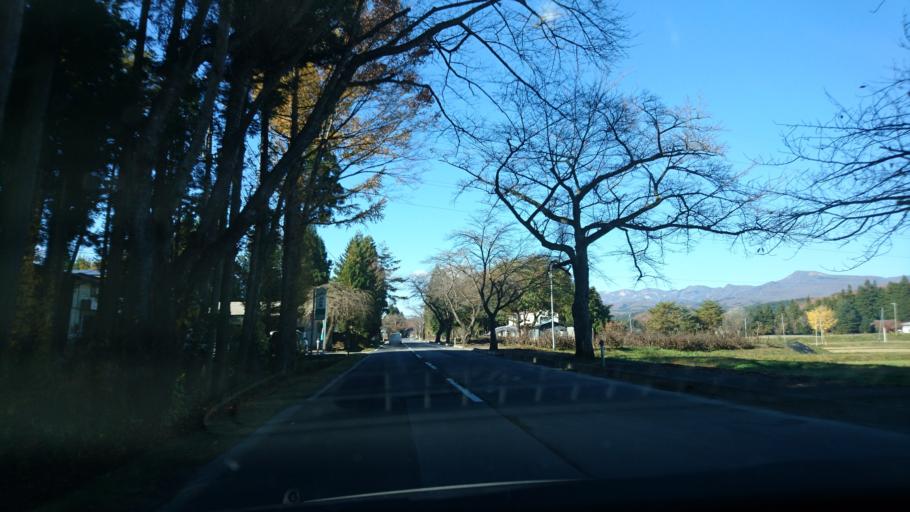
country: JP
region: Iwate
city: Mizusawa
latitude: 39.1264
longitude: 141.0025
